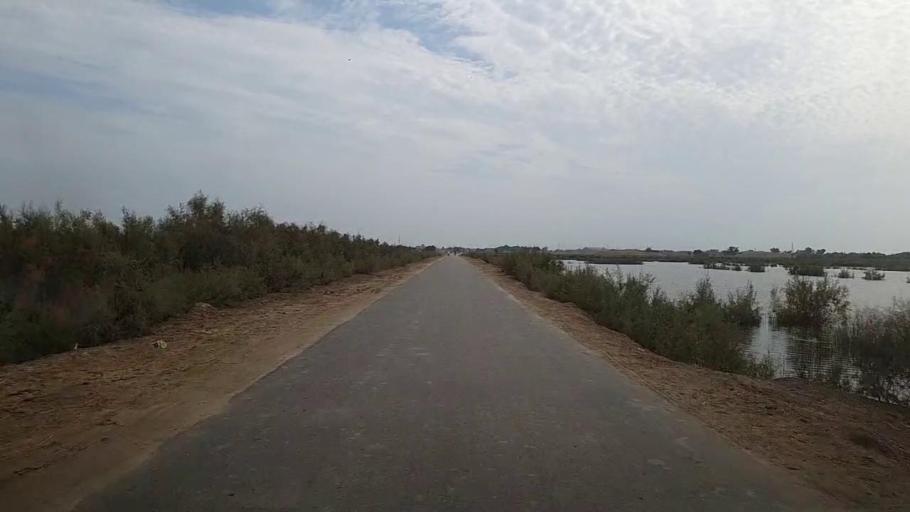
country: PK
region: Sindh
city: Thul
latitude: 28.2636
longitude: 68.7785
